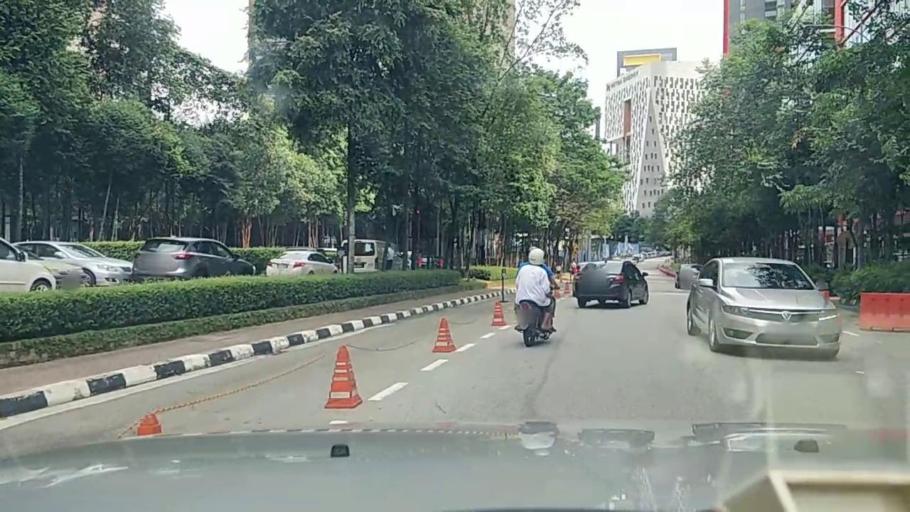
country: MY
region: Selangor
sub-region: Petaling
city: Petaling Jaya
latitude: 3.1678
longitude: 101.6128
